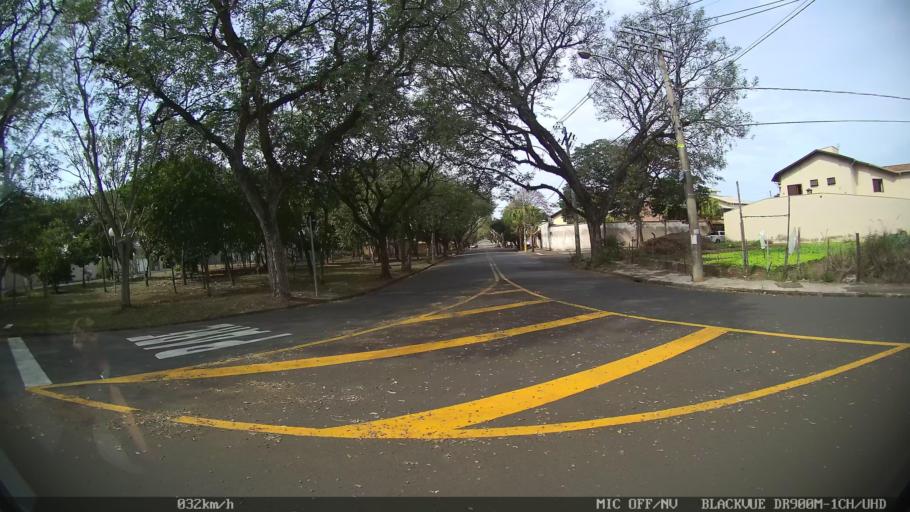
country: BR
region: Sao Paulo
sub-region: Piracicaba
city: Piracicaba
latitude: -22.7115
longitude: -47.6757
